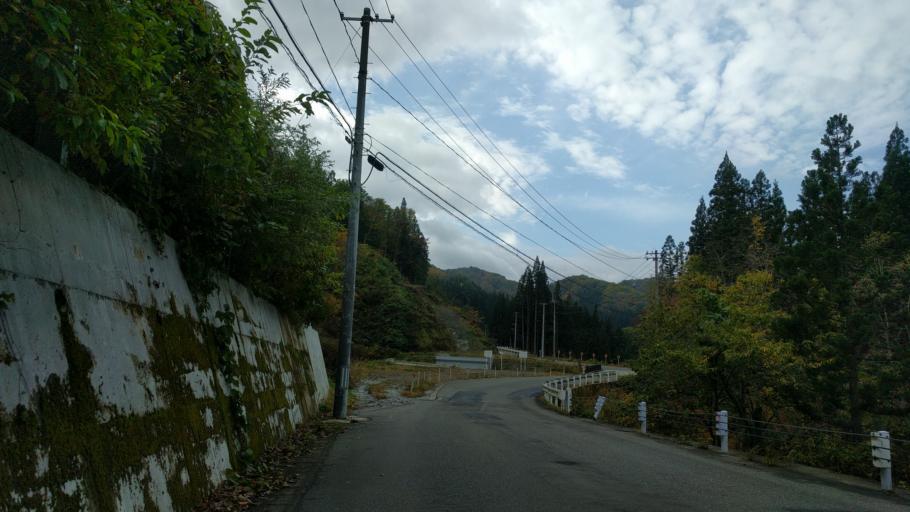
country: JP
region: Fukushima
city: Kitakata
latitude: 37.4020
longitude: 139.6965
